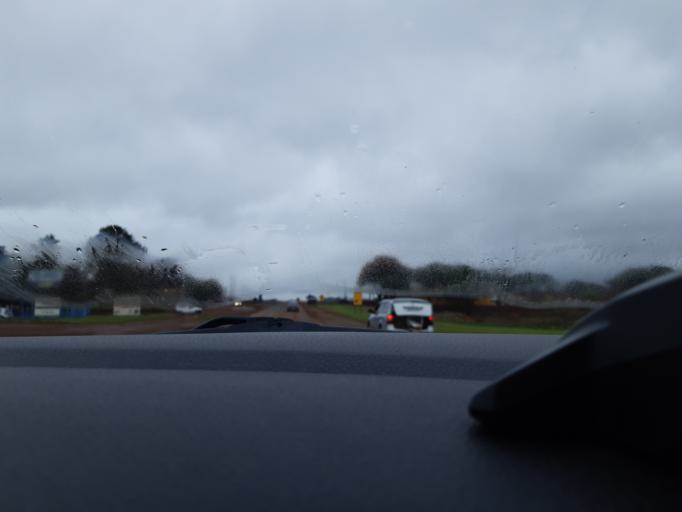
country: BR
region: Parana
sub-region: Bandeirantes
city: Bandeirantes
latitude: -23.0552
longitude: -50.2438
